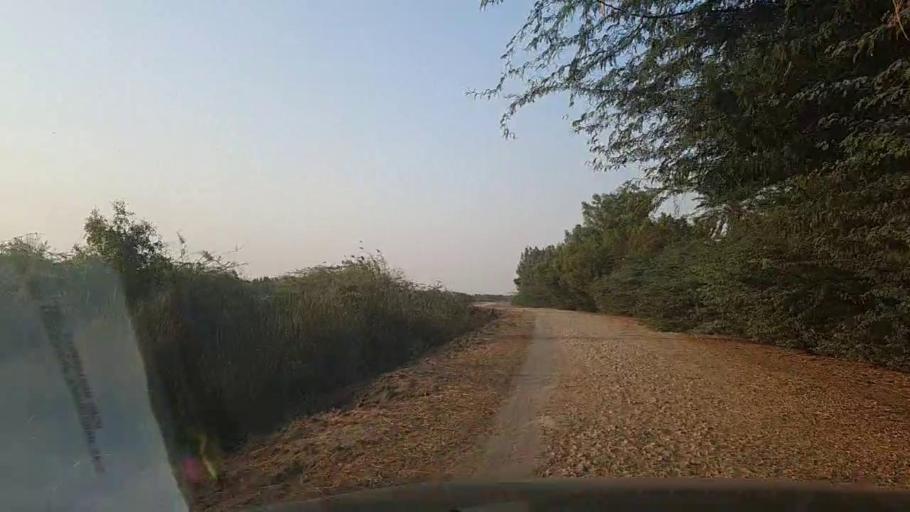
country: PK
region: Sindh
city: Keti Bandar
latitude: 24.3145
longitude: 67.5994
